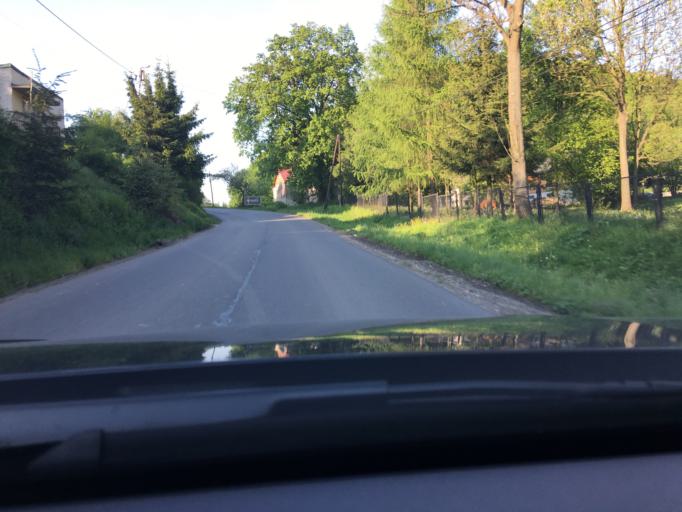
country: PL
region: Lesser Poland Voivodeship
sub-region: Powiat krakowski
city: Jerzmanowice
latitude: 50.2031
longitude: 19.7354
